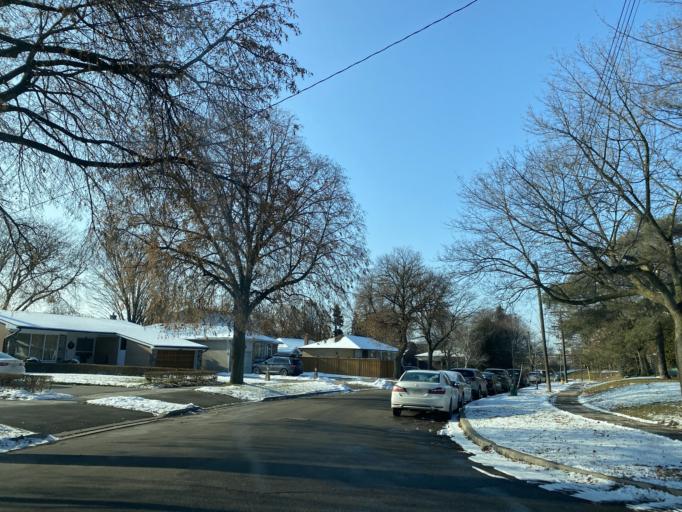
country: CA
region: Ontario
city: Etobicoke
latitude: 43.6722
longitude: -79.5669
